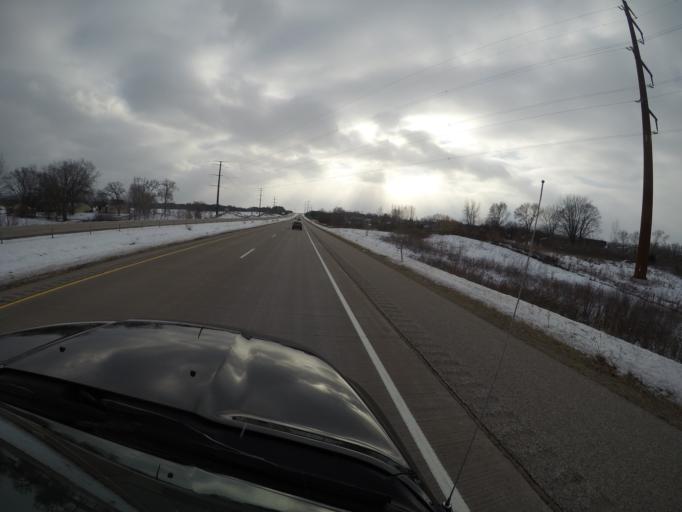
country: US
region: Wisconsin
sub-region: La Crosse County
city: Holmen
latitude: 43.9817
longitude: -91.2864
